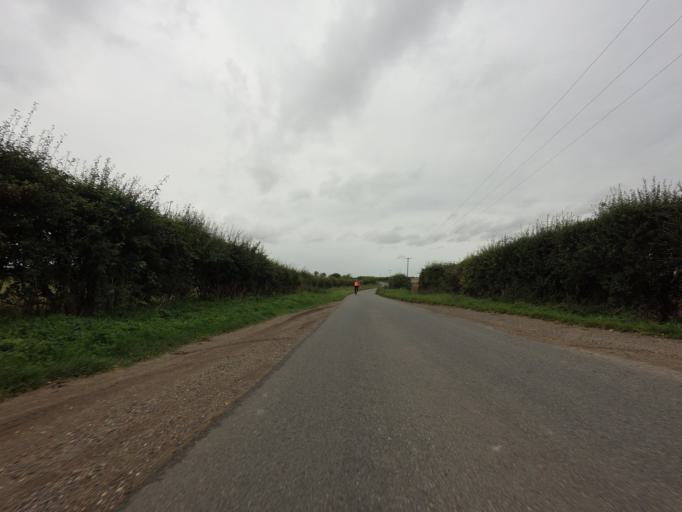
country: GB
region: England
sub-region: Cambridgeshire
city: Duxford
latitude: 52.0461
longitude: 0.1574
